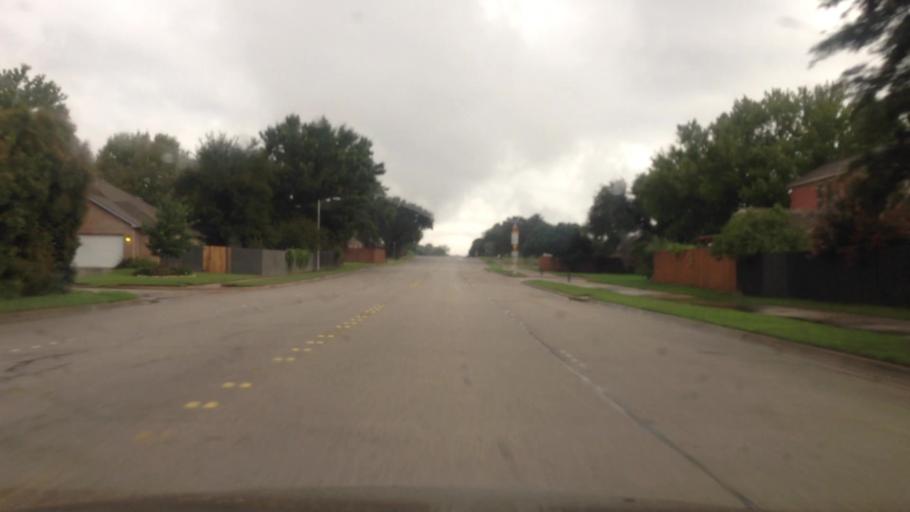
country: US
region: Texas
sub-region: Tarrant County
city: North Richland Hills
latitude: 32.8638
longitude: -97.2033
